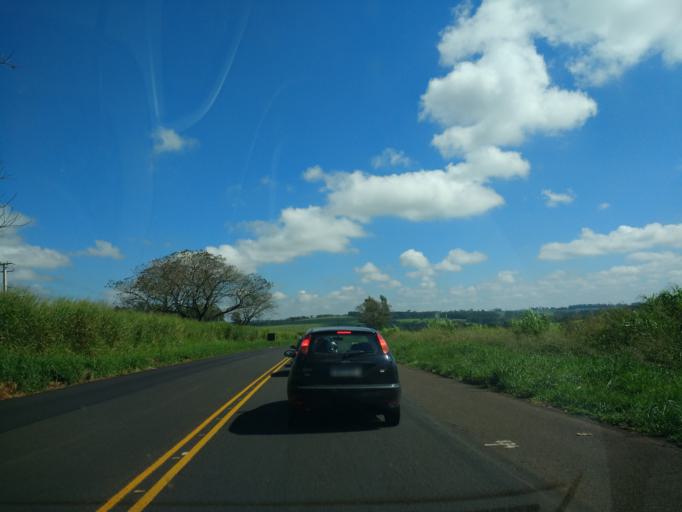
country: BR
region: Parana
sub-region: Cianorte
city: Cianorte
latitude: -23.7355
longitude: -52.7196
